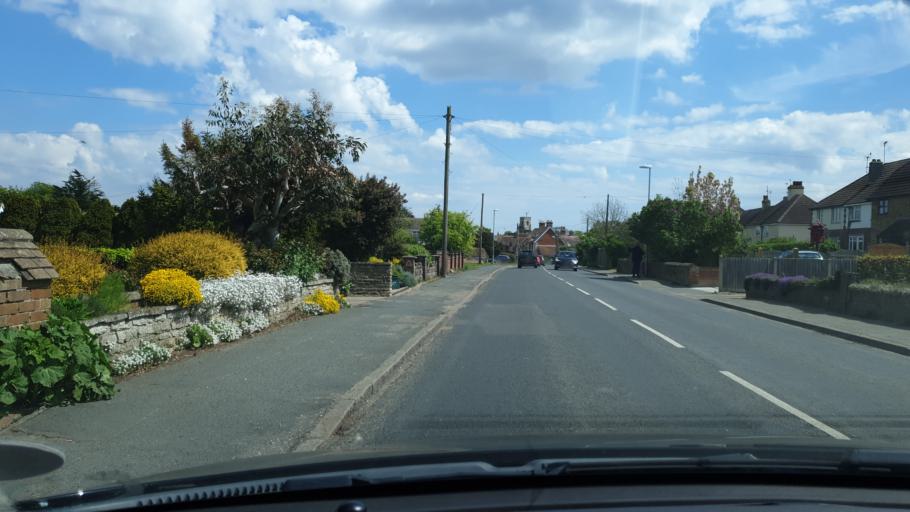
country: GB
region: England
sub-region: Essex
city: Walton-on-the-Naze
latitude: 51.8490
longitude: 1.2610
